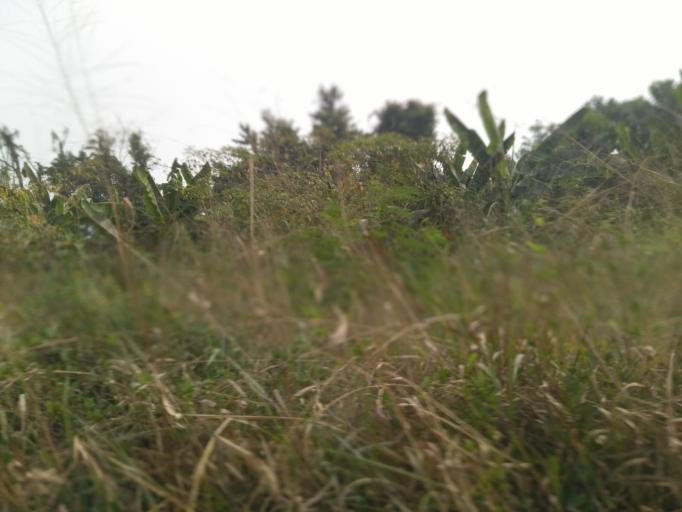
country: GH
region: Ashanti
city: Kumasi
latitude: 6.6738
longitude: -1.6295
